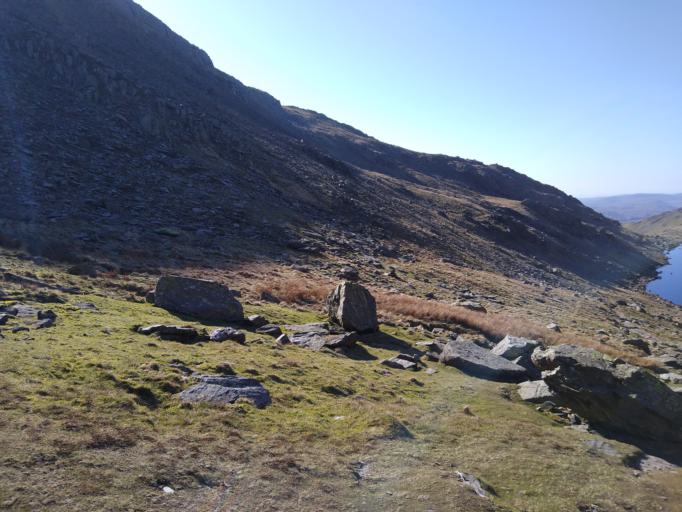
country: GB
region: England
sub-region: Cumbria
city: Ambleside
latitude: 54.3721
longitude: -3.1302
